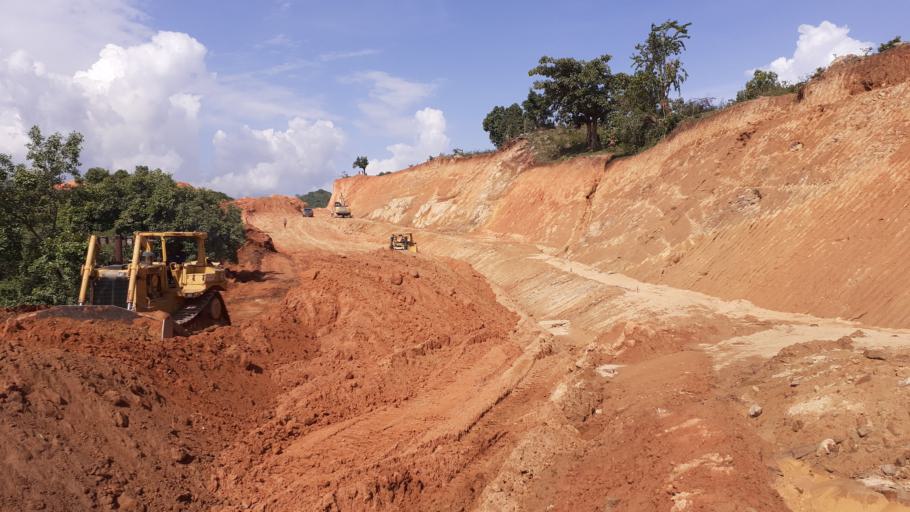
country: ET
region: Oromiya
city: Gimbi
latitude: 9.3333
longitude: 35.6941
